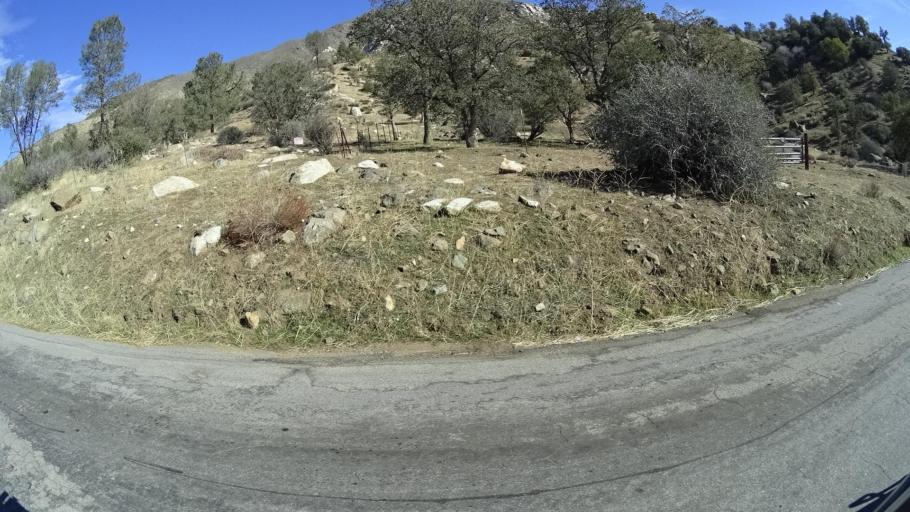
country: US
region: California
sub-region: Kern County
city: Bodfish
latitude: 35.5455
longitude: -118.5075
